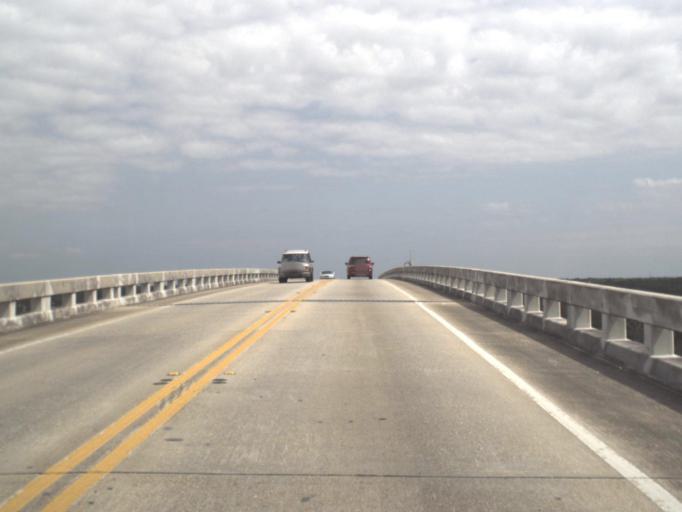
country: US
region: Alabama
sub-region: Baldwin County
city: Orange Beach
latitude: 30.3119
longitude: -87.4266
